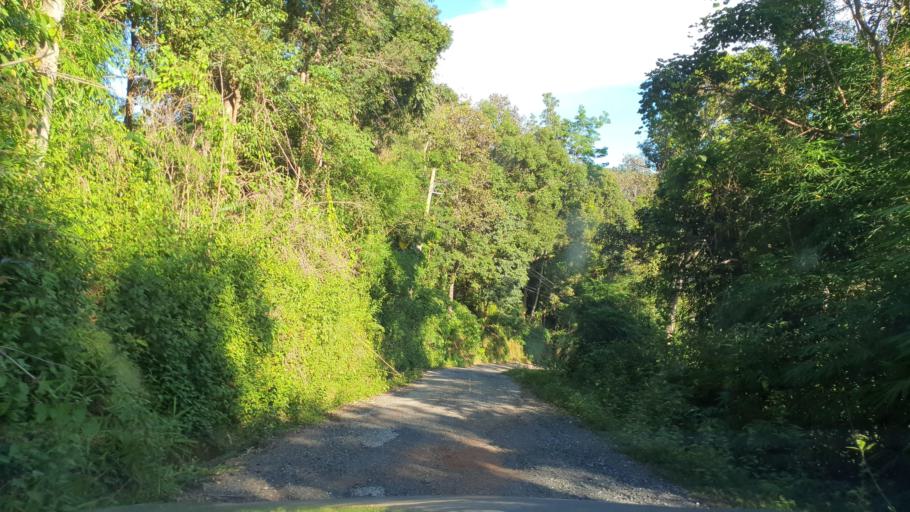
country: TH
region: Chiang Mai
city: Mae On
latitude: 18.8114
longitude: 99.3275
